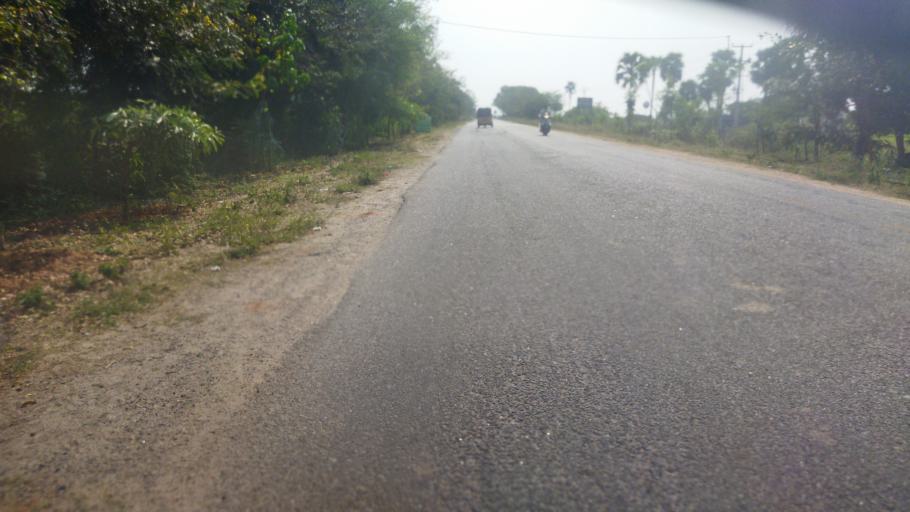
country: IN
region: Telangana
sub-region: Nalgonda
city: Nalgonda
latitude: 17.1045
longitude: 79.2817
